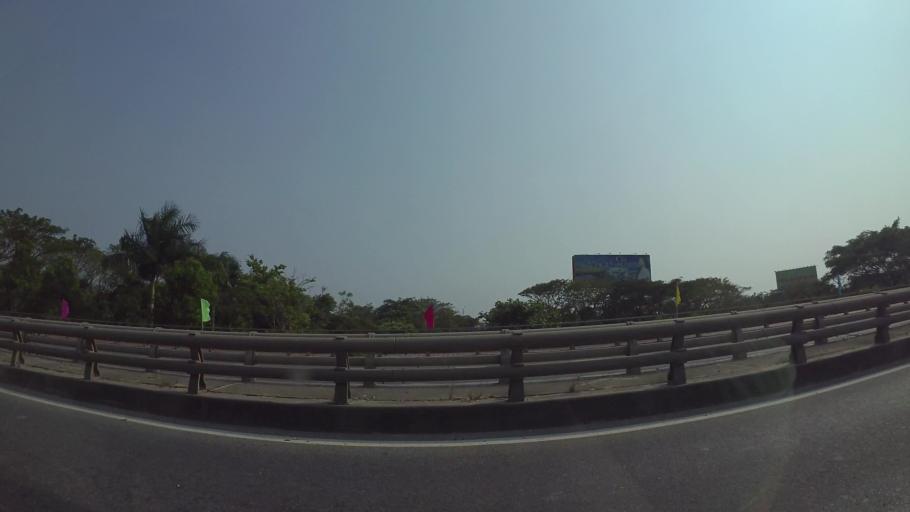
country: VN
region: Da Nang
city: Cam Le
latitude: 16.0144
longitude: 108.1932
